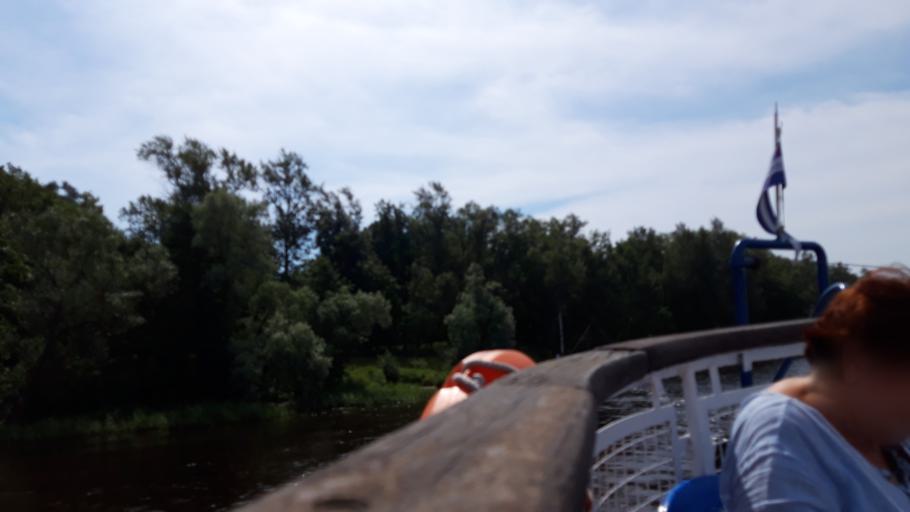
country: RU
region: Tverskaya
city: Konakovo
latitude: 56.6900
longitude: 36.6977
